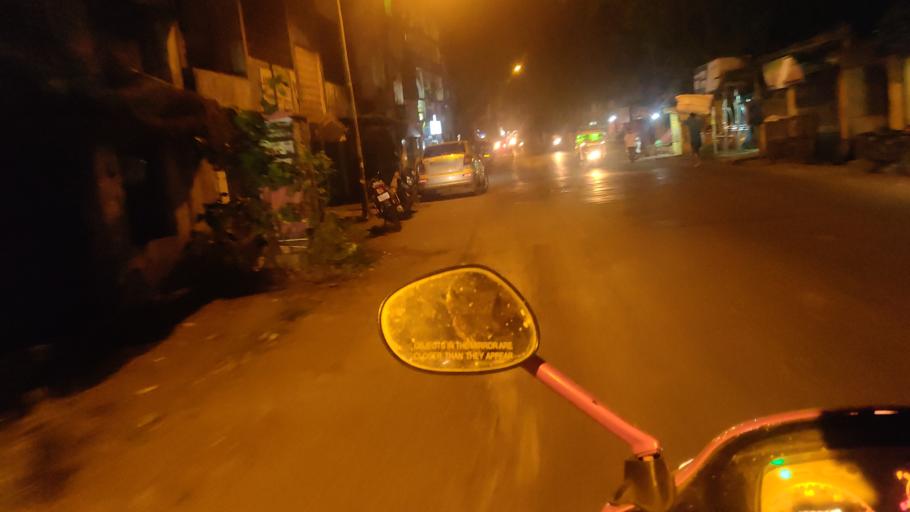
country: IN
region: Maharashtra
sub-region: Thane
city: Bhayandar
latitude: 19.2995
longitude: 72.8308
